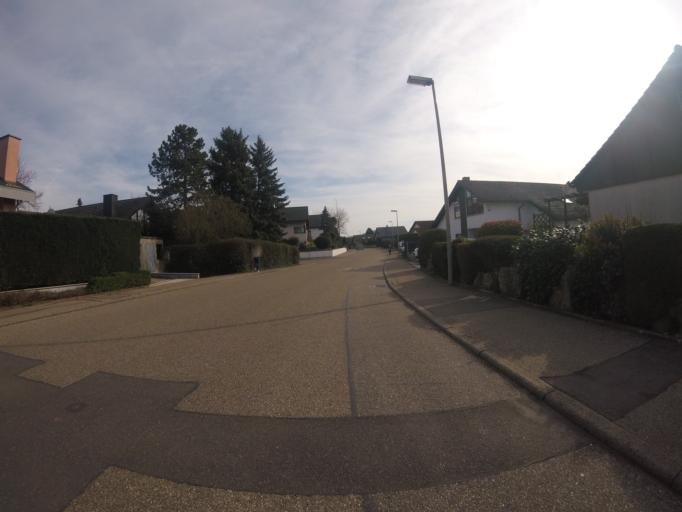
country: DE
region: Baden-Wuerttemberg
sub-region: Regierungsbezirk Stuttgart
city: Abstatt
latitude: 49.0596
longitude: 9.2899
